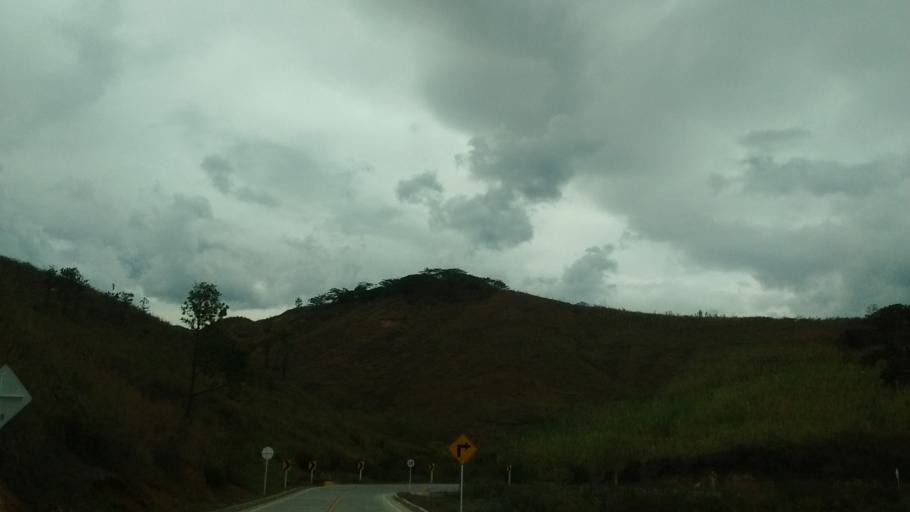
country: CO
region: Cauca
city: La Sierra
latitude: 2.1490
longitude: -76.7813
